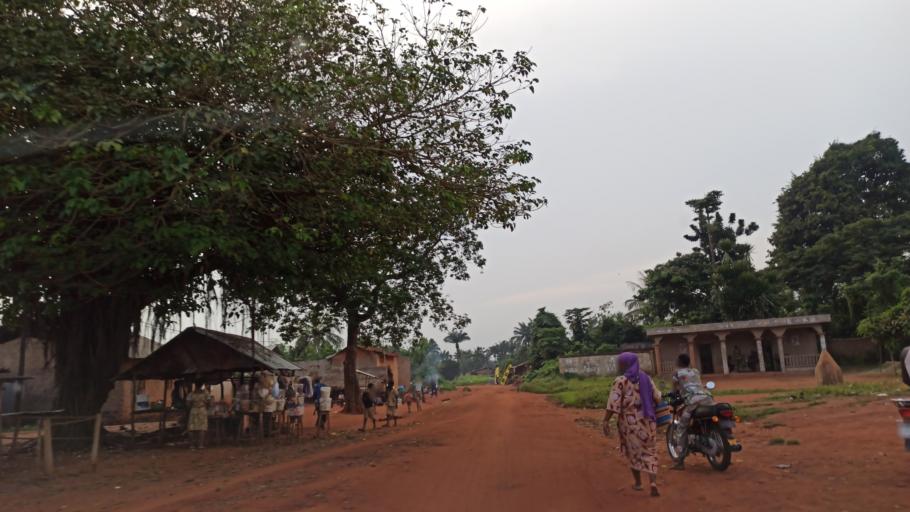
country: BJ
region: Queme
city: Porto-Novo
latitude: 6.5349
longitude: 2.6548
